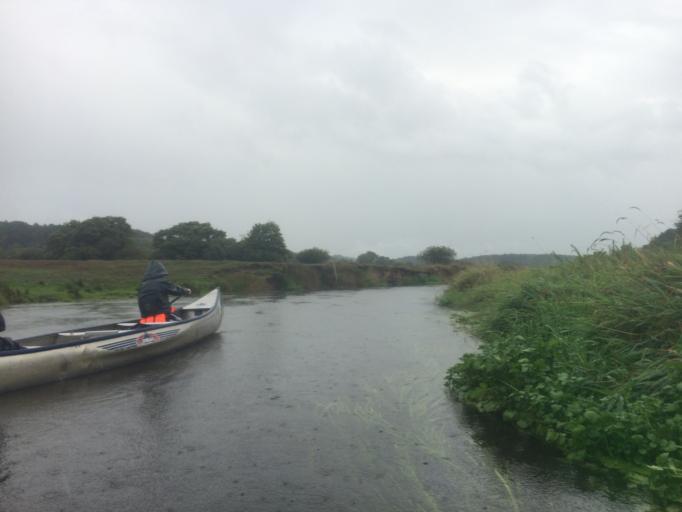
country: DK
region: South Denmark
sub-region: Vejle Kommune
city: Egtved
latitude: 55.6722
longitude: 9.3521
